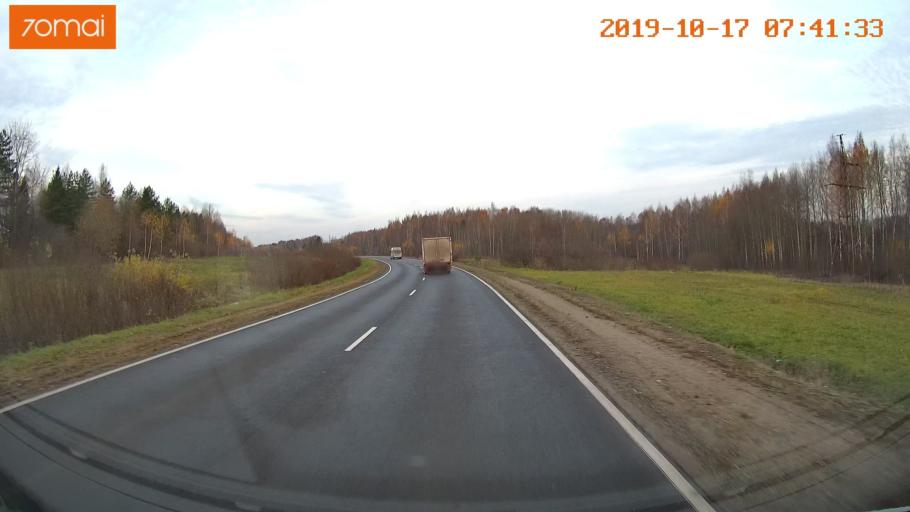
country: RU
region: Vladimir
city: Yur'yev-Pol'skiy
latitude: 56.4826
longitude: 39.8078
